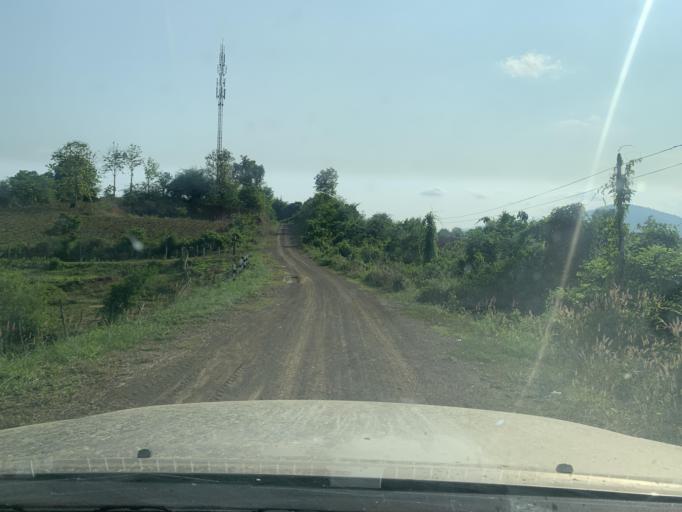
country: TH
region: Uttaradit
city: Ban Khok
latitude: 18.2855
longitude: 101.3184
